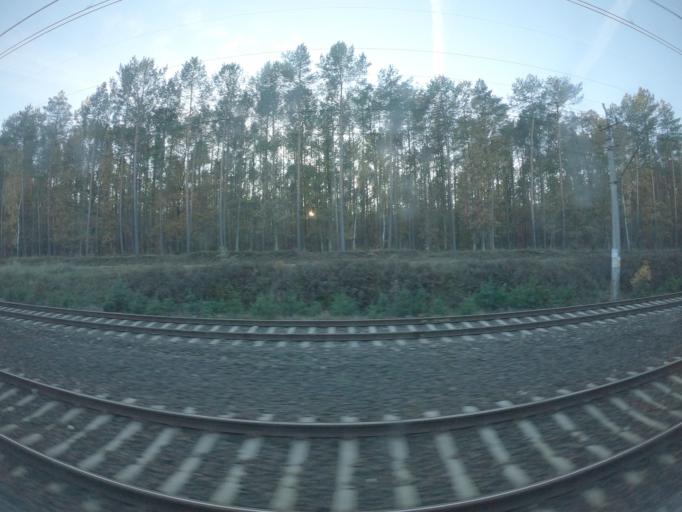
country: PL
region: Lubusz
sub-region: Powiat slubicki
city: Rzepin
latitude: 52.3155
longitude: 14.8567
